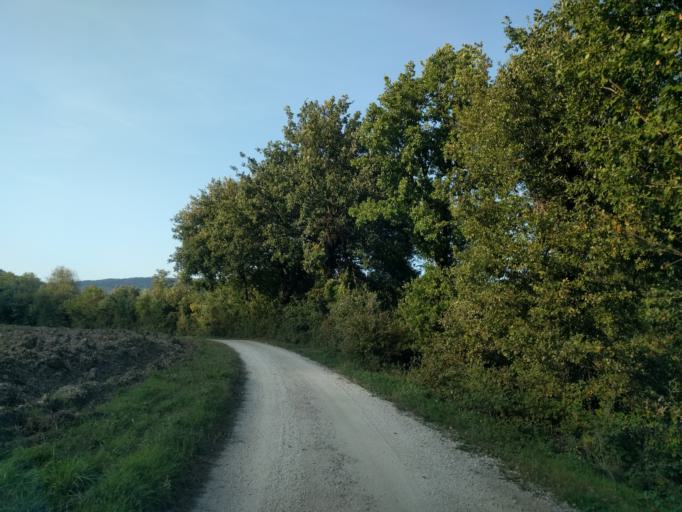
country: IT
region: The Marches
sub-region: Provincia di Pesaro e Urbino
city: Canavaccio
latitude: 43.6948
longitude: 12.6887
